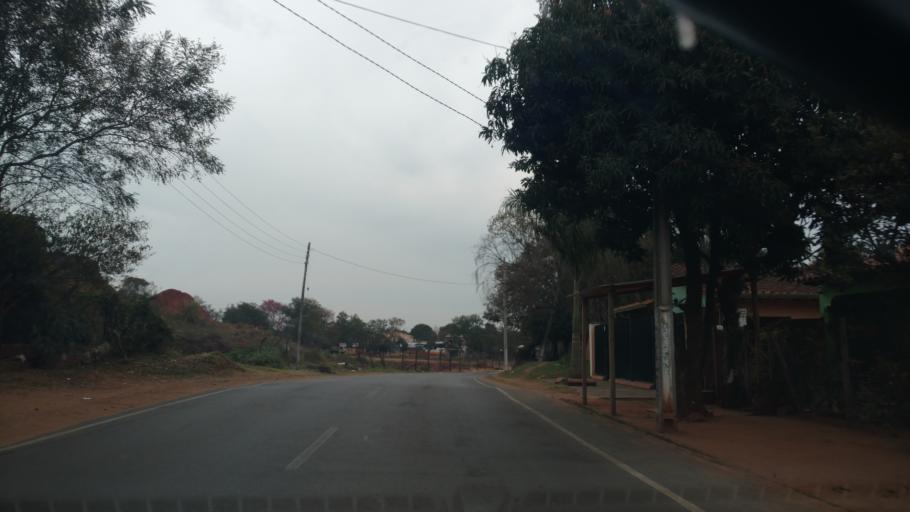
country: PY
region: Central
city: Capiata
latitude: -25.3581
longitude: -57.4776
